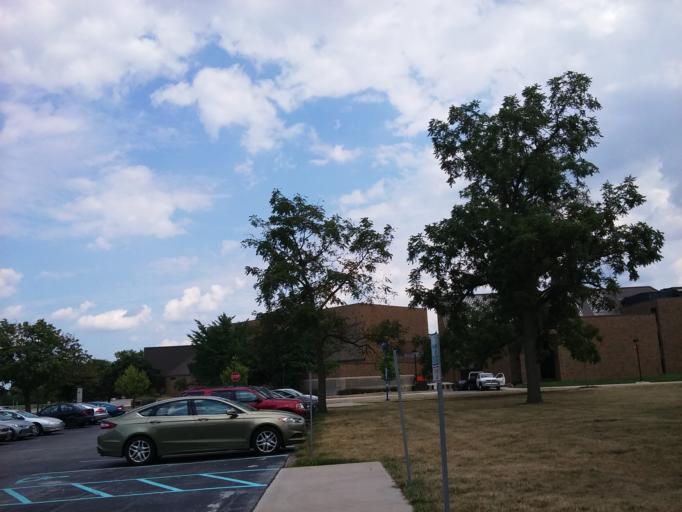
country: US
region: Ohio
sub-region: Wood County
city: Bowling Green
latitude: 41.3792
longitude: -83.6349
